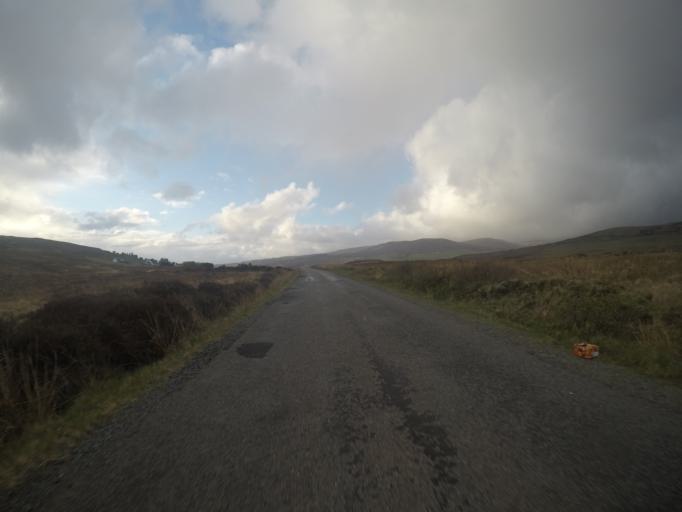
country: GB
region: Scotland
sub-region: Highland
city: Isle of Skye
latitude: 57.4614
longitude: -6.2965
